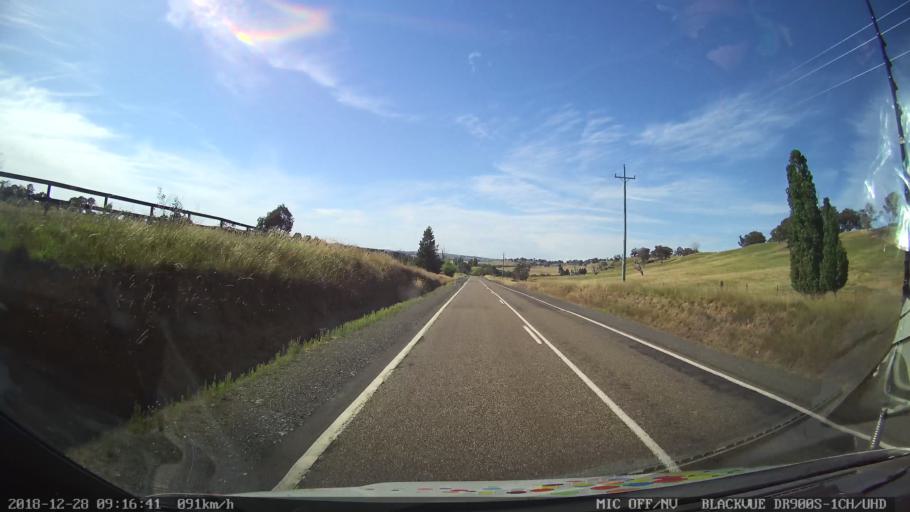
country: AU
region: New South Wales
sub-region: Upper Lachlan Shire
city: Crookwell
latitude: -34.3119
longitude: 149.3567
